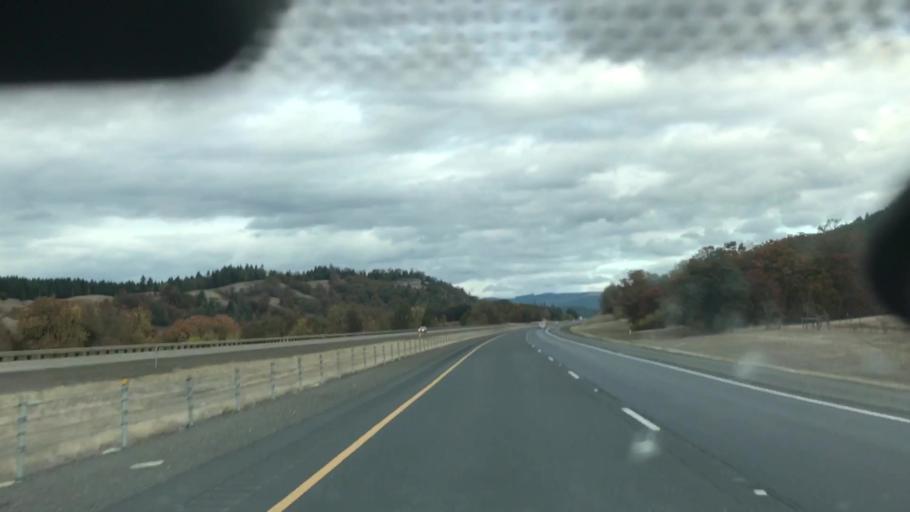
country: US
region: Oregon
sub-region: Douglas County
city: Yoncalla
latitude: 43.5911
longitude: -123.2493
